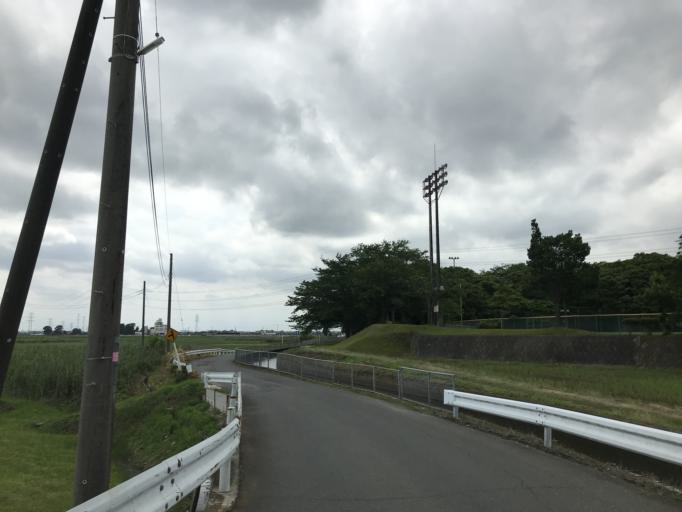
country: JP
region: Ibaraki
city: Moriya
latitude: 35.9784
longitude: 140.0467
